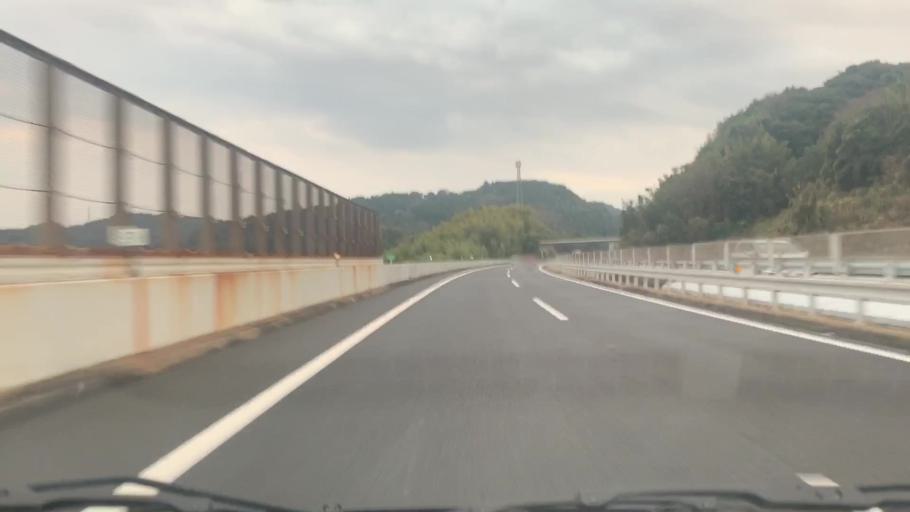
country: JP
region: Nagasaki
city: Omura
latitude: 32.8878
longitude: 129.9929
